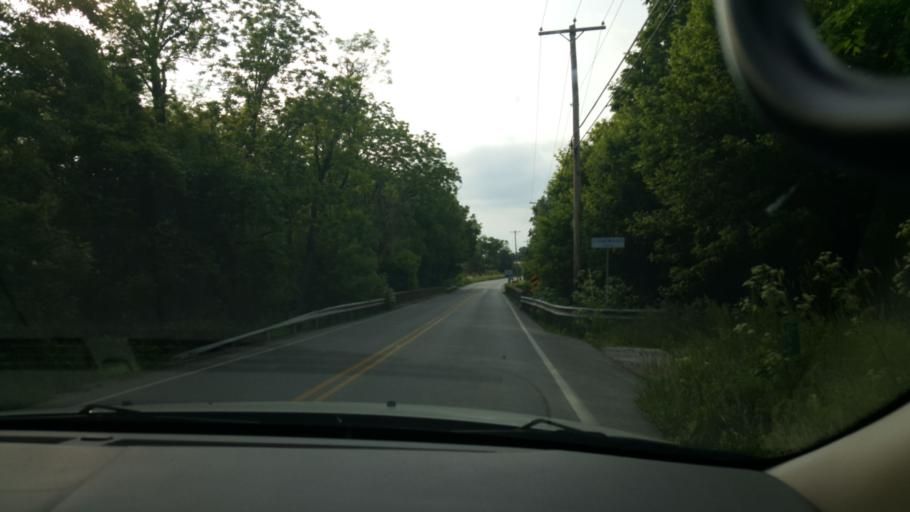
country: US
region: Pennsylvania
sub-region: York County
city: Shiloh
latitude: 40.0003
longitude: -76.7983
